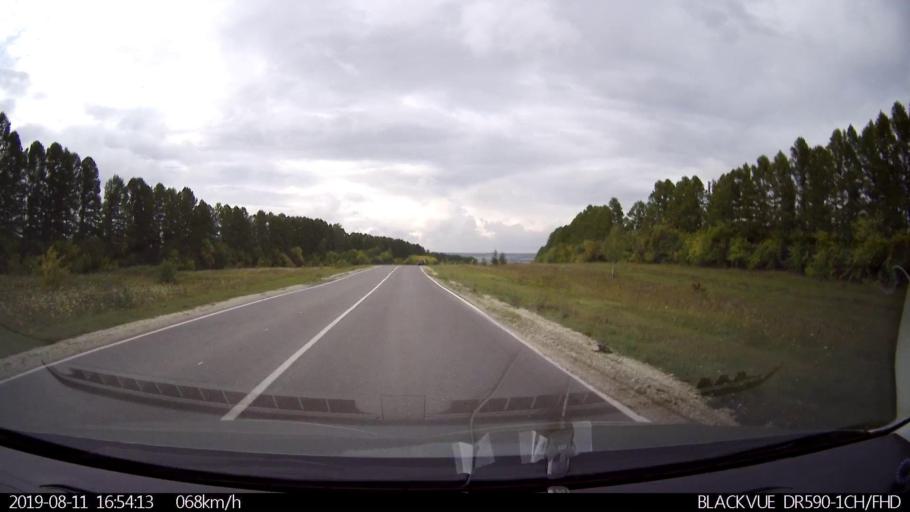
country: RU
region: Ulyanovsk
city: Mayna
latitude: 54.2704
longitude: 47.6668
